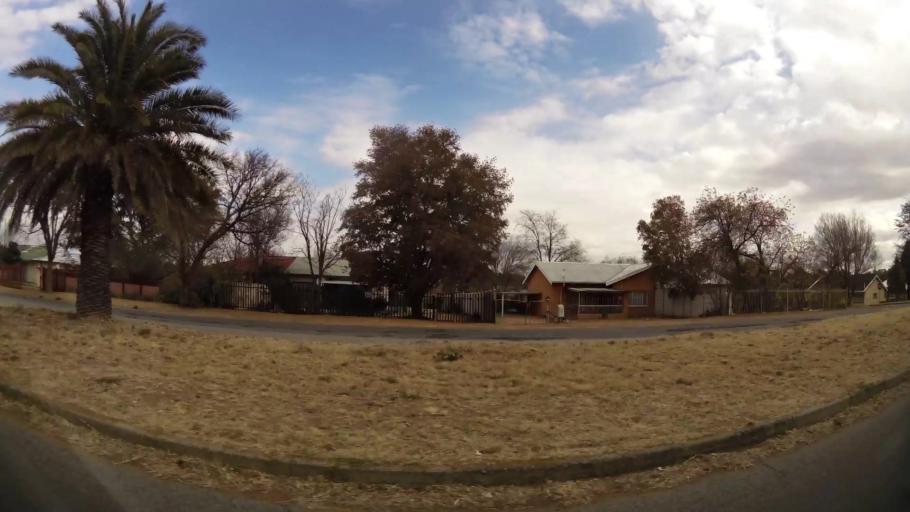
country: ZA
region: Orange Free State
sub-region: Fezile Dabi District Municipality
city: Kroonstad
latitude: -27.6437
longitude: 27.2278
